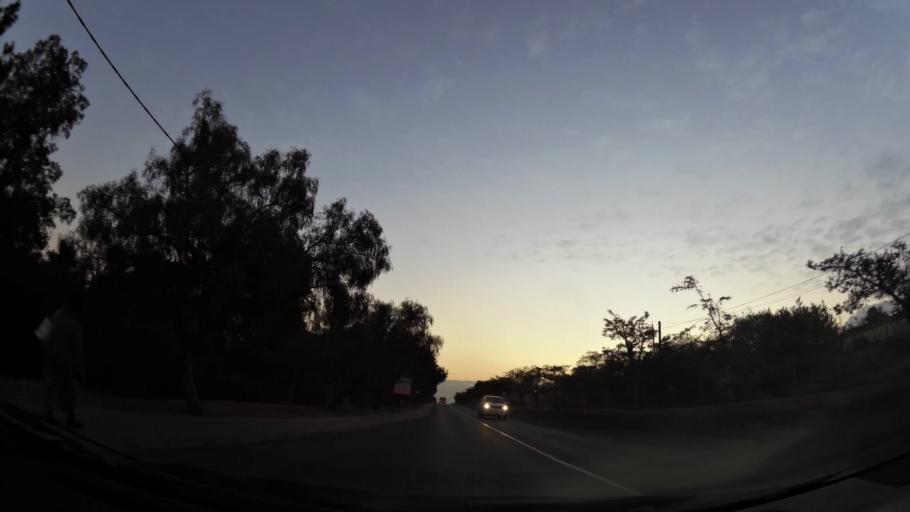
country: ZA
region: Gauteng
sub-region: City of Johannesburg Metropolitan Municipality
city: Midrand
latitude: -25.9746
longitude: 28.0759
